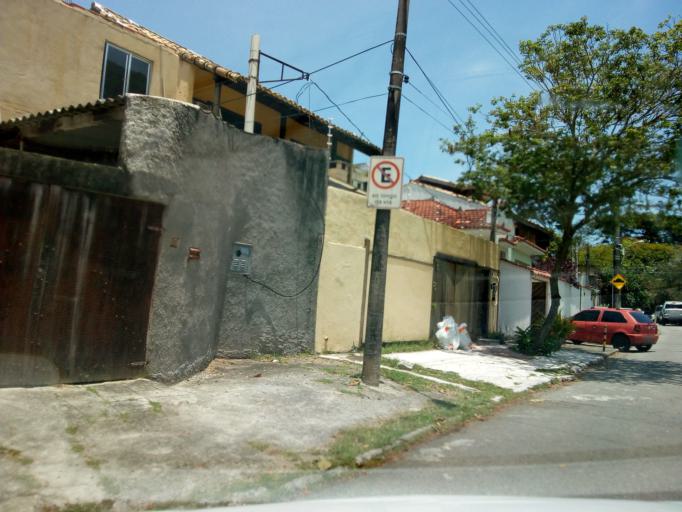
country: BR
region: Rio de Janeiro
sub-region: Rio De Janeiro
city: Rio de Janeiro
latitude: -23.0075
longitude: -43.2959
